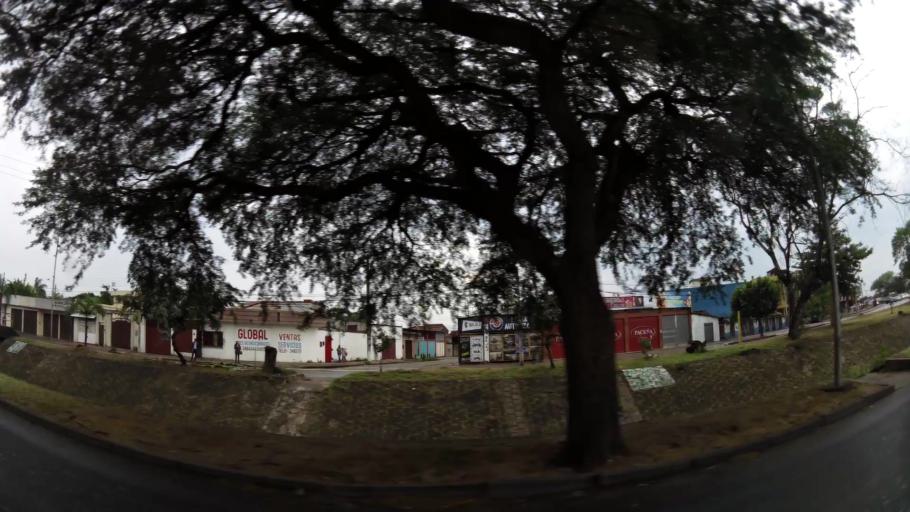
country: BO
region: Santa Cruz
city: Santa Cruz de la Sierra
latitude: -17.7800
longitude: -63.1484
